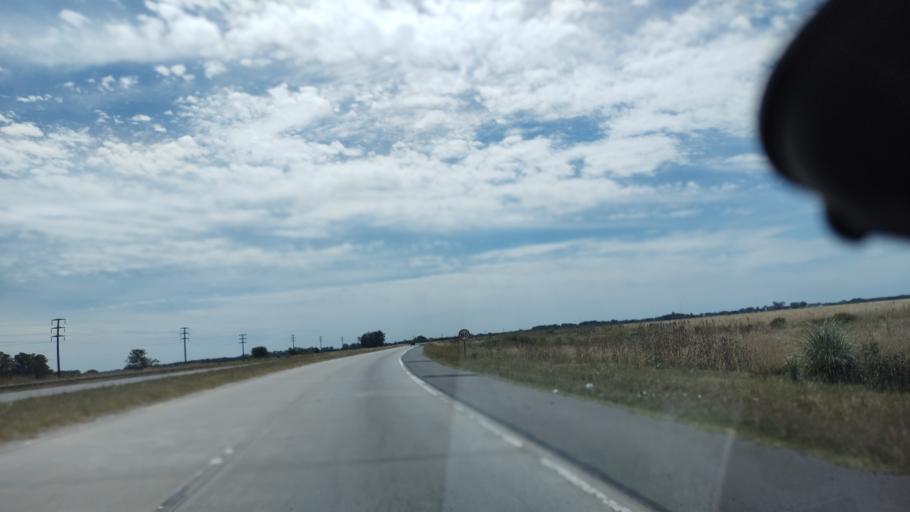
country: AR
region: Buenos Aires
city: Canuelas
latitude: -35.0753
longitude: -58.6896
